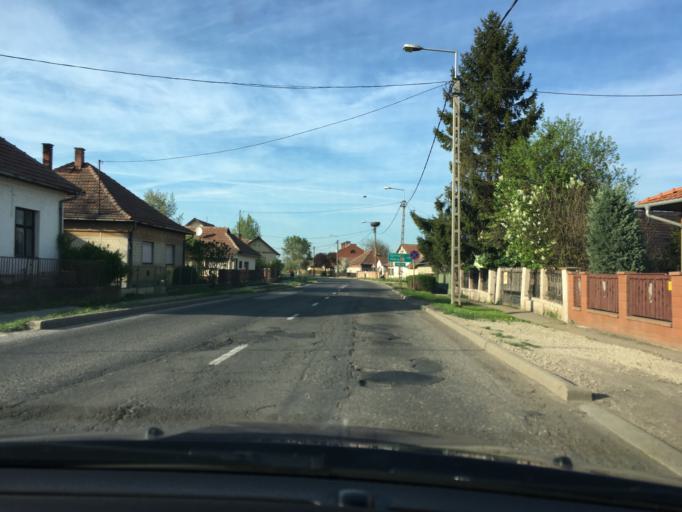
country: HU
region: Hajdu-Bihar
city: Csokmo
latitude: 47.0309
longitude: 21.2955
